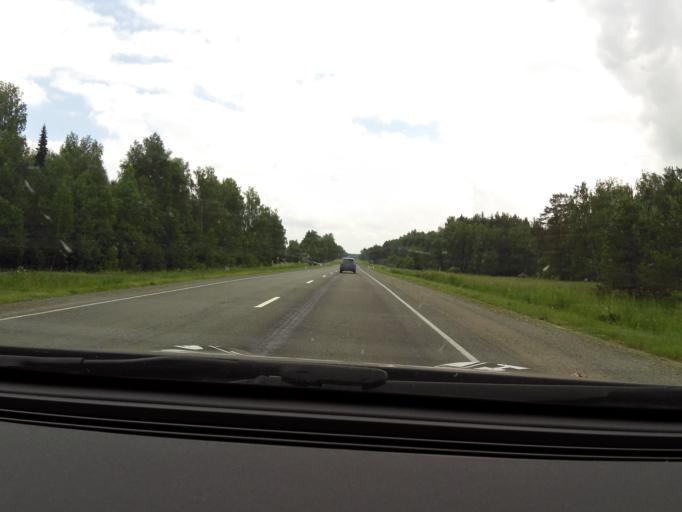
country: RU
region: Perm
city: Suksun
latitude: 56.9196
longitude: 57.5717
